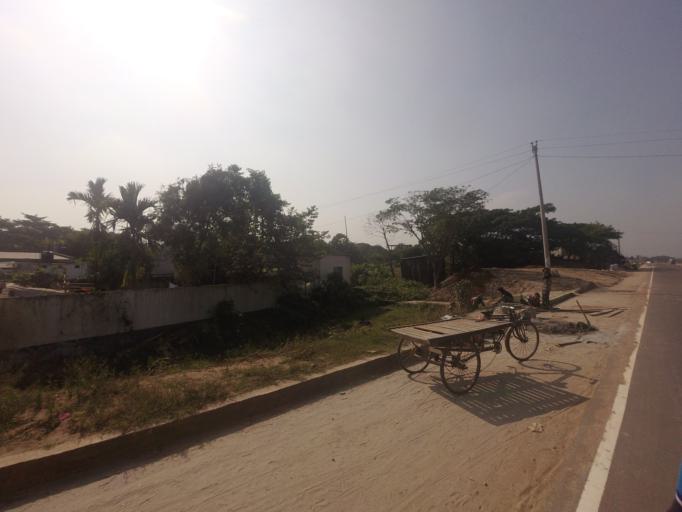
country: BD
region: Dhaka
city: Azimpur
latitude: 23.7346
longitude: 90.3310
